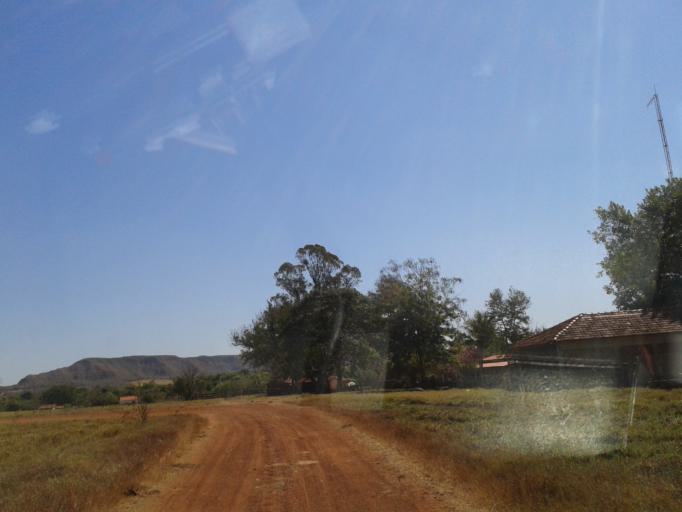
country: BR
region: Minas Gerais
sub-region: Santa Vitoria
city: Santa Vitoria
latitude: -19.0651
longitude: -50.0554
